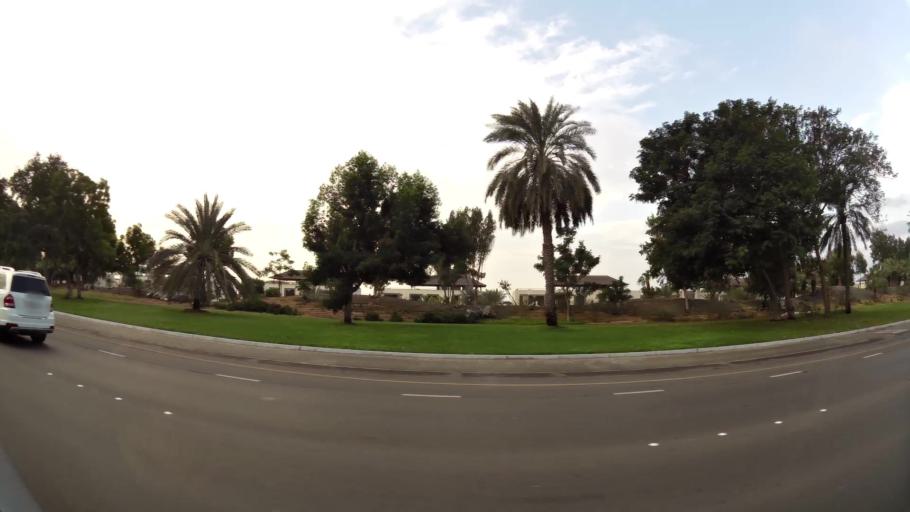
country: AE
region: Abu Dhabi
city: Abu Dhabi
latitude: 24.4266
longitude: 54.4018
